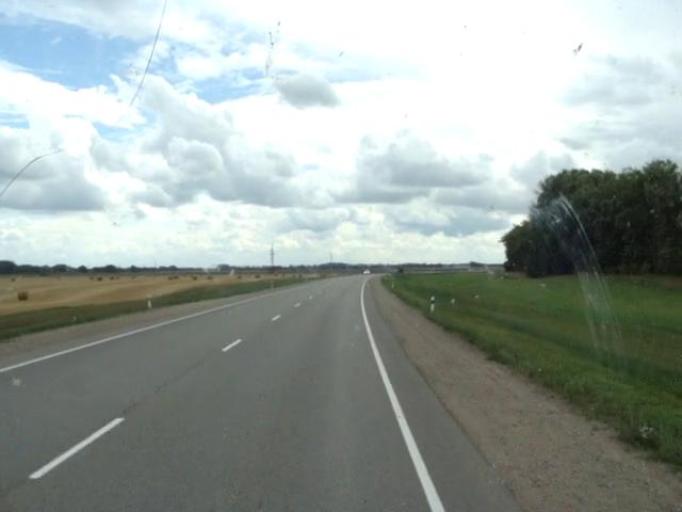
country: RU
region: Altai Krai
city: Shubenka
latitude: 52.6815
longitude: 85.0473
